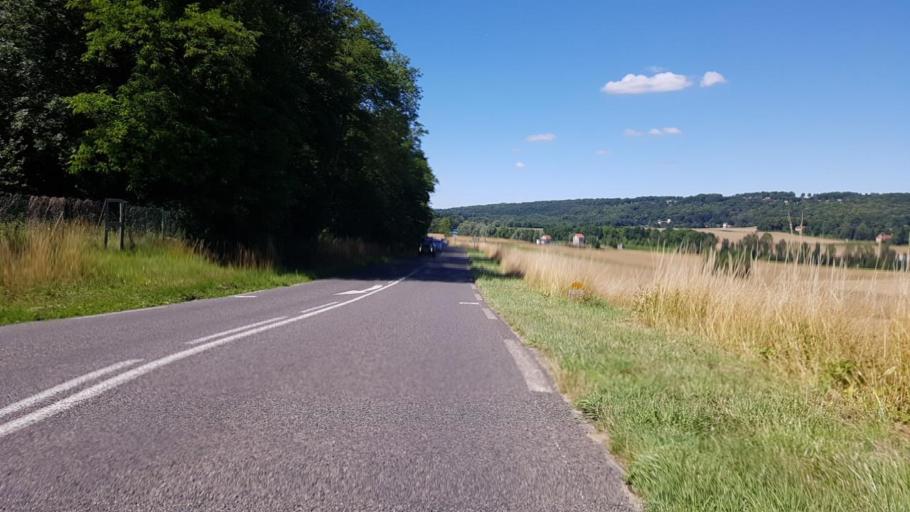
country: FR
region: Ile-de-France
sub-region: Departement de Seine-et-Marne
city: Chamigny
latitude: 48.9709
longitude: 3.1722
